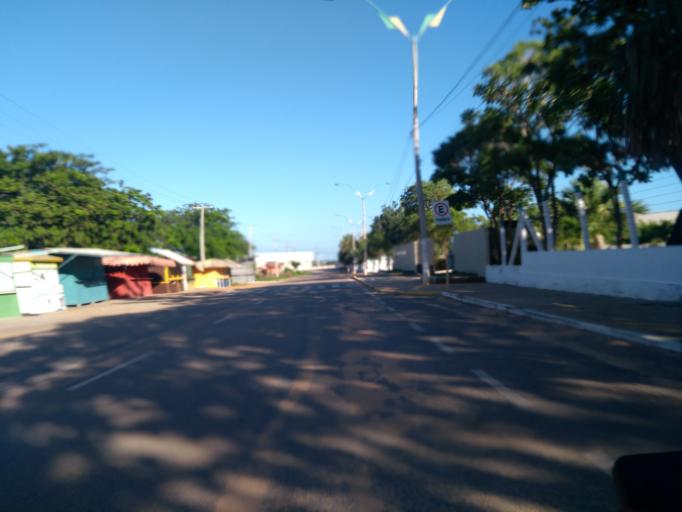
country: BR
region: Ceara
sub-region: Aracati
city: Aracati
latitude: -4.5711
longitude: -37.7934
